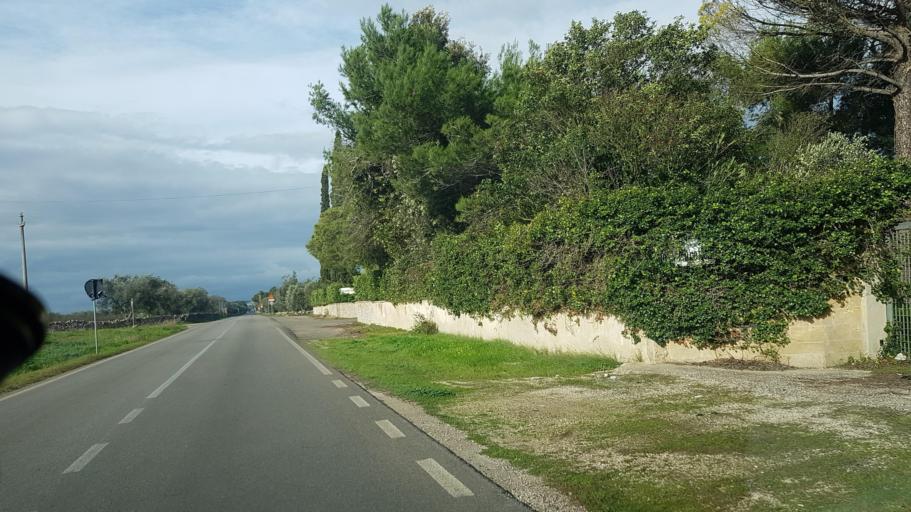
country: IT
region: Apulia
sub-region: Provincia di Brindisi
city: Oria
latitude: 40.4805
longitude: 17.6889
